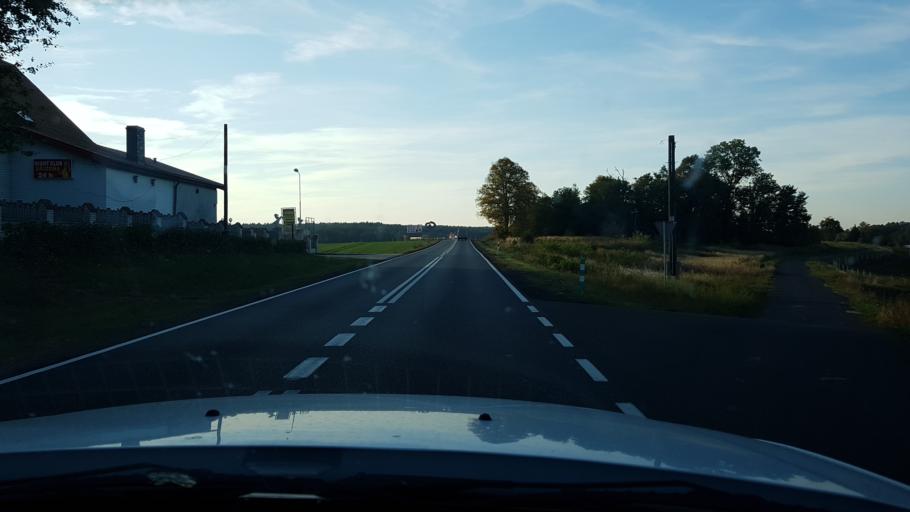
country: PL
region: West Pomeranian Voivodeship
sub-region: Powiat gryfinski
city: Chojna
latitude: 52.9647
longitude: 14.4047
